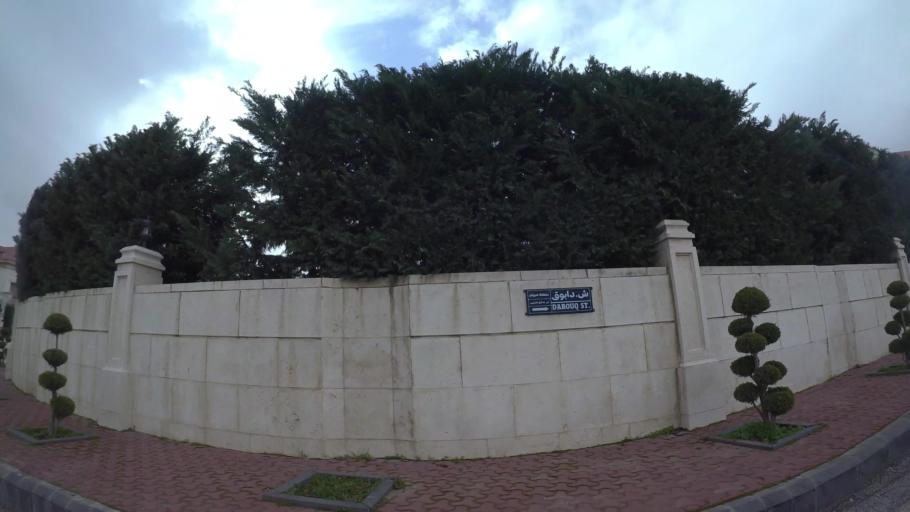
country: JO
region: Amman
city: Wadi as Sir
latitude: 31.9921
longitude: 35.8225
